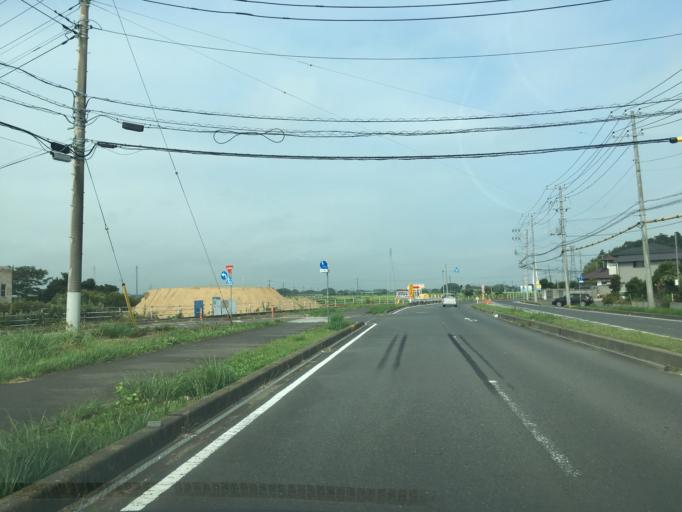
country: JP
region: Ibaraki
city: Oarai
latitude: 36.3504
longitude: 140.5748
